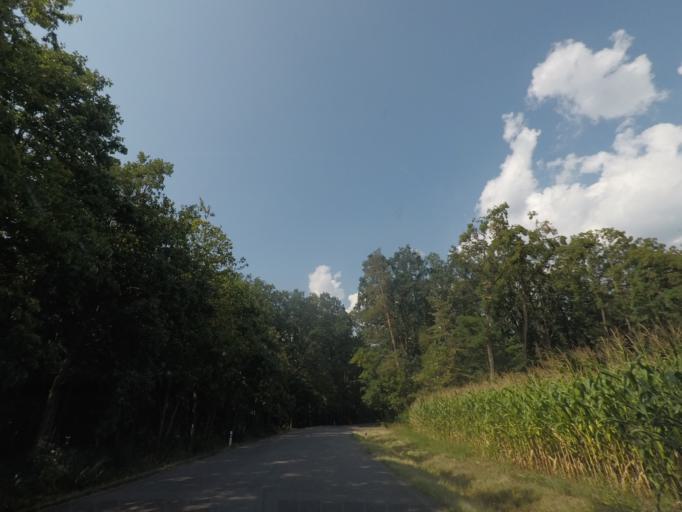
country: CZ
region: Pardubicky
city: Horni Jeleni
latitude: 50.0602
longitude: 16.0819
